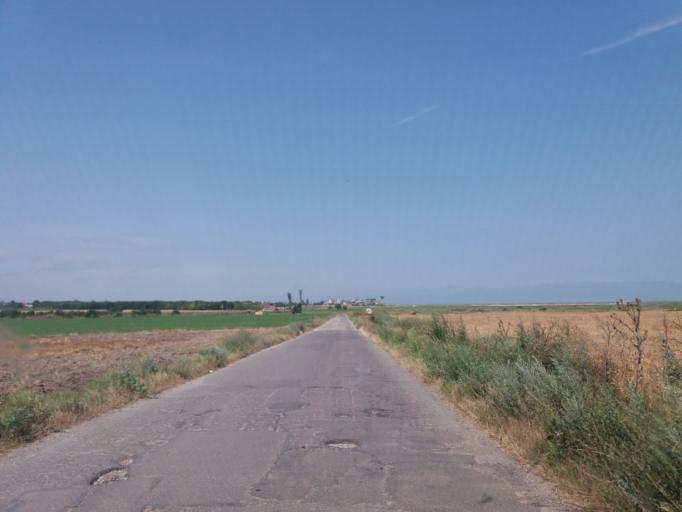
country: RO
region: Constanta
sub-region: Comuna Sacele
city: Sacele
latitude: 44.4365
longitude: 28.7238
